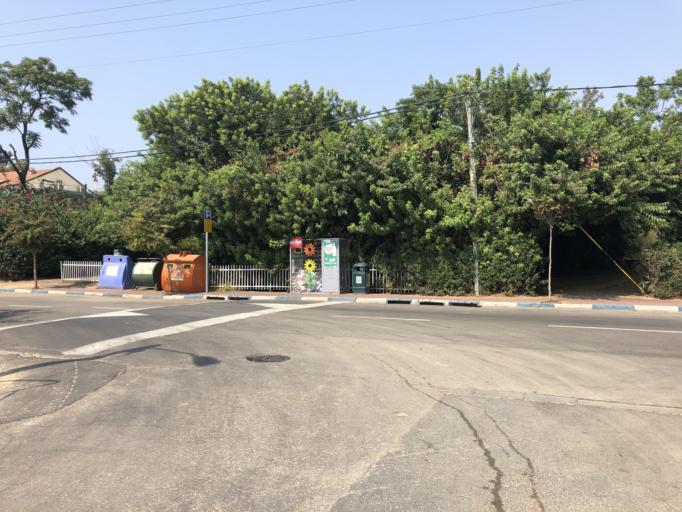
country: IL
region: Tel Aviv
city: Giv`atayim
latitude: 32.0569
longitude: 34.8305
